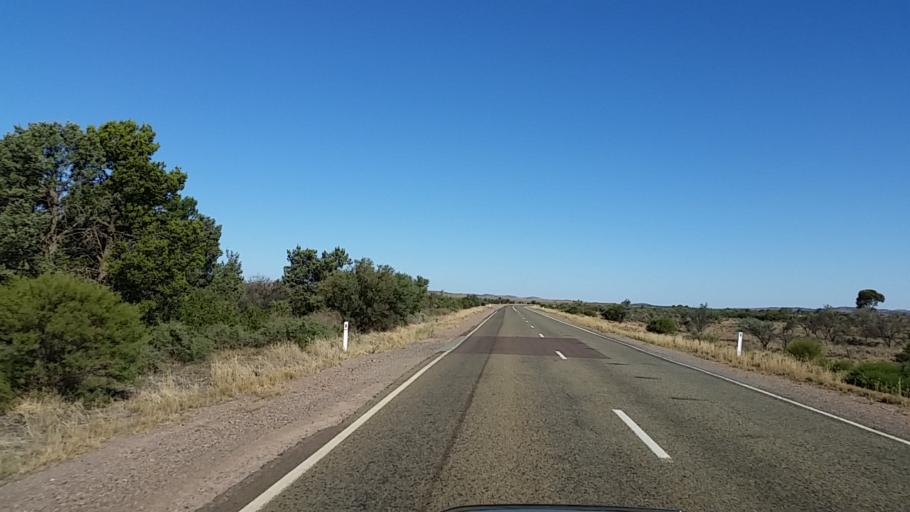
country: AU
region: South Australia
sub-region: Flinders Ranges
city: Quorn
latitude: -32.4352
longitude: 138.5339
